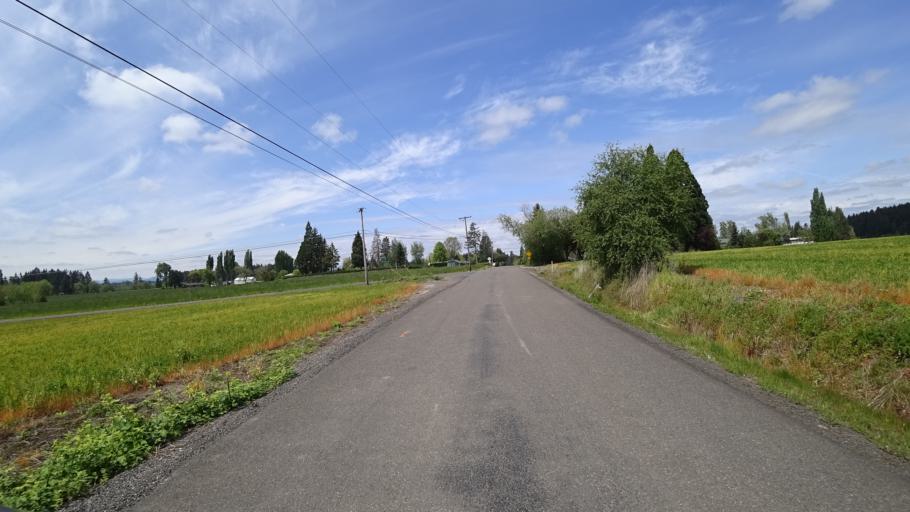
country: US
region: Oregon
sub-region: Washington County
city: North Plains
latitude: 45.5662
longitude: -122.9494
